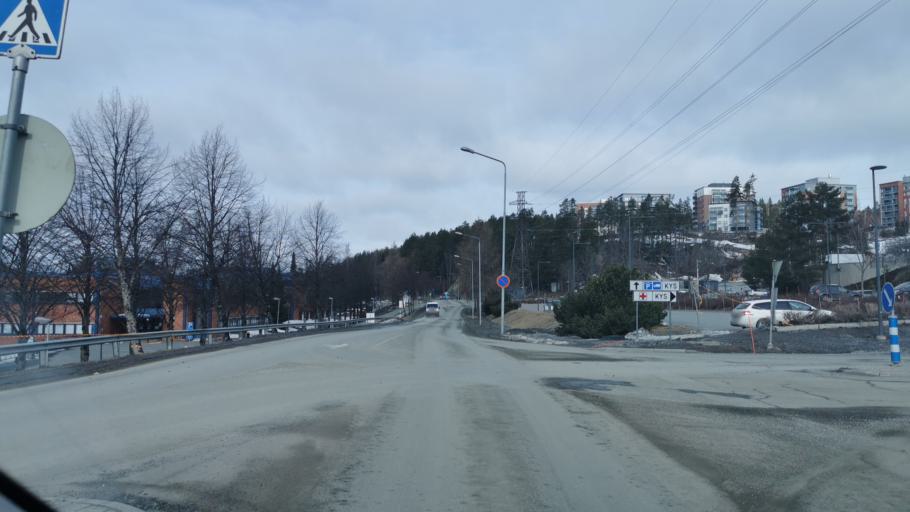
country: FI
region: Northern Savo
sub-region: Kuopio
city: Kuopio
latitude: 62.8960
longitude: 27.6447
